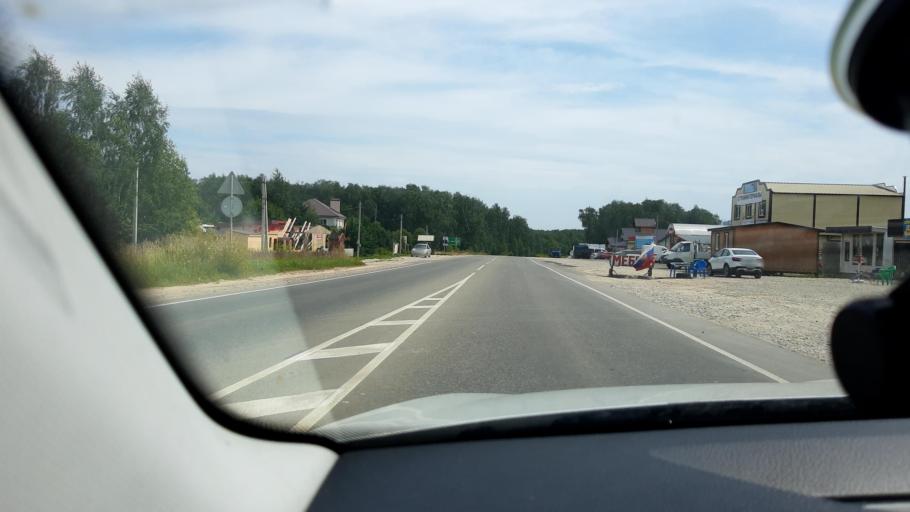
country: RU
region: Tula
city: Zaokskiy
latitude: 54.7459
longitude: 37.4102
